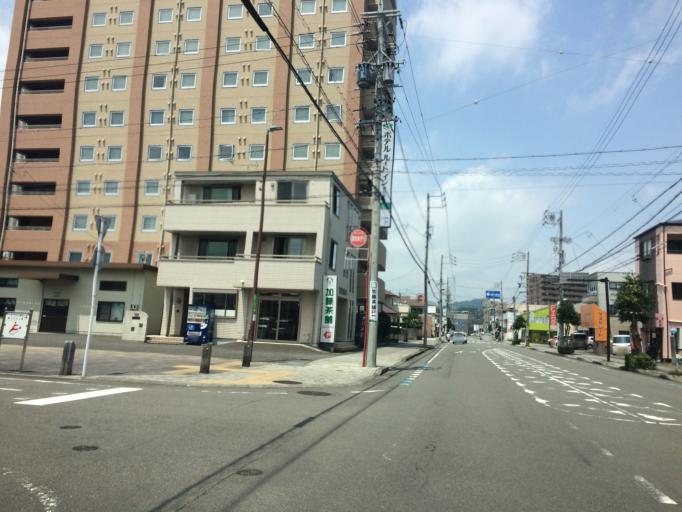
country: JP
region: Shizuoka
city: Fujieda
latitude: 34.8539
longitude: 138.2502
